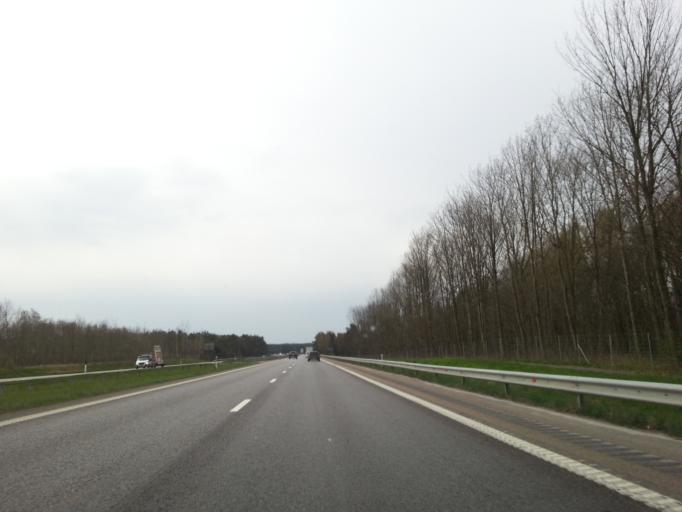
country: SE
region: Halland
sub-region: Laholms Kommun
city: Mellbystrand
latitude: 56.5352
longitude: 12.9683
